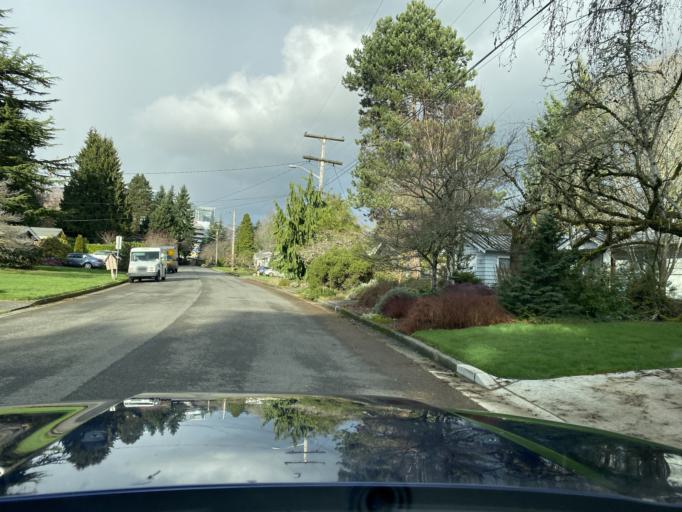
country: US
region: Washington
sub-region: King County
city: Bellevue
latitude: 47.6067
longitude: -122.1929
